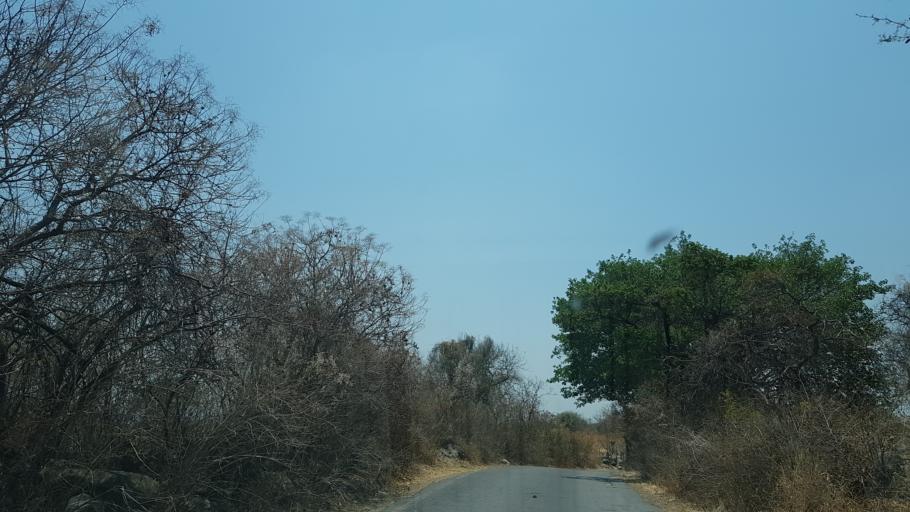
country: MX
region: Puebla
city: Huaquechula
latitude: 18.7859
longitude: -98.5449
